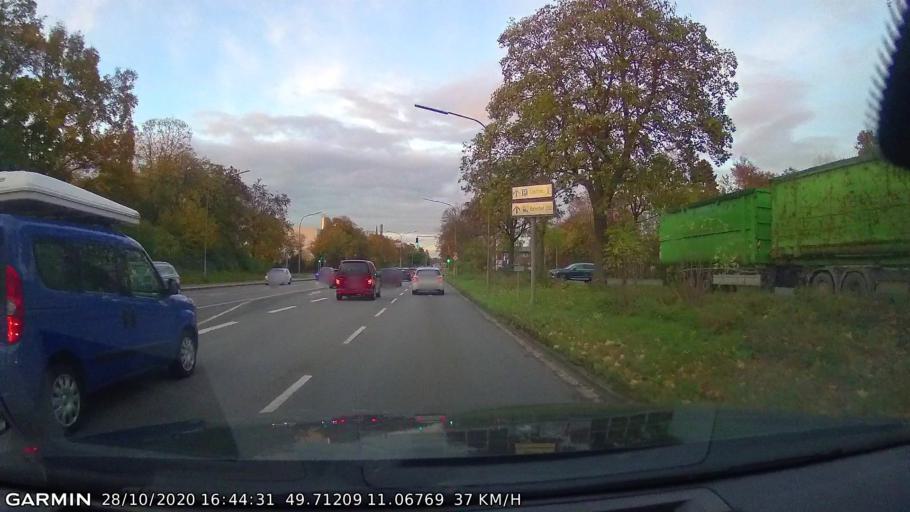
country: DE
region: Bavaria
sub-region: Upper Franconia
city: Forchheim
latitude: 49.7122
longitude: 11.0677
